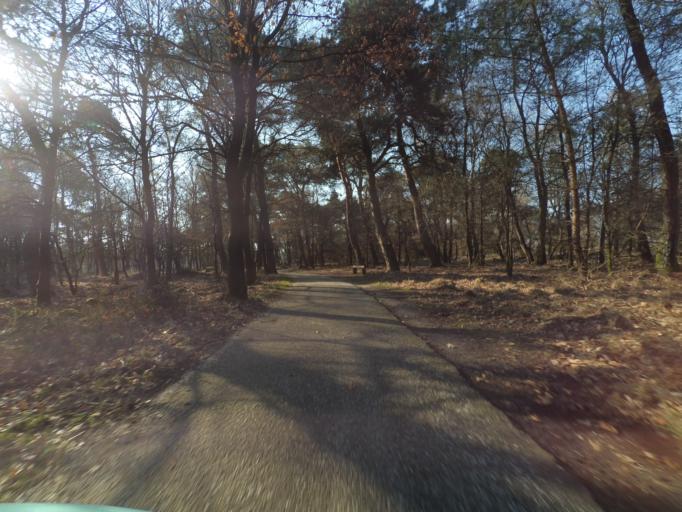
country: NL
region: Gelderland
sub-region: Gemeente Arnhem
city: Hoogkamp
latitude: 52.0604
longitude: 5.8513
